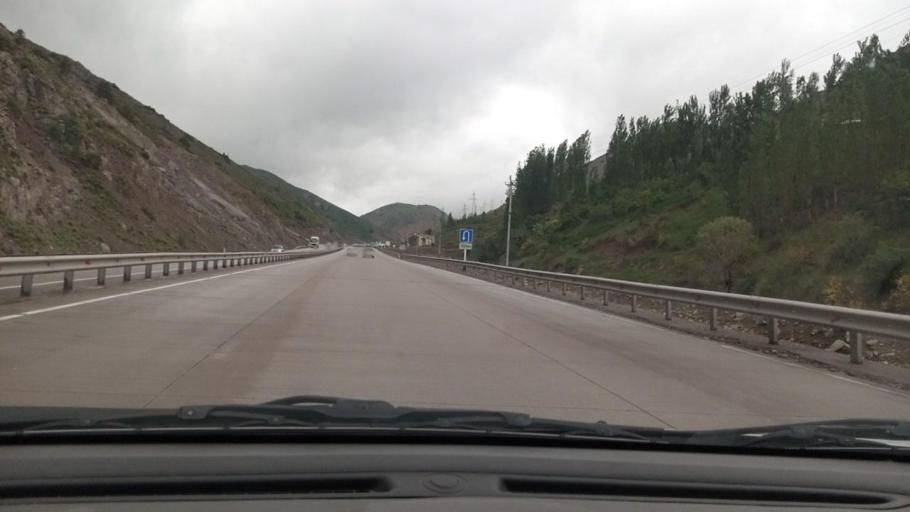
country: UZ
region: Toshkent
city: Angren
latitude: 41.0478
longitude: 70.5708
